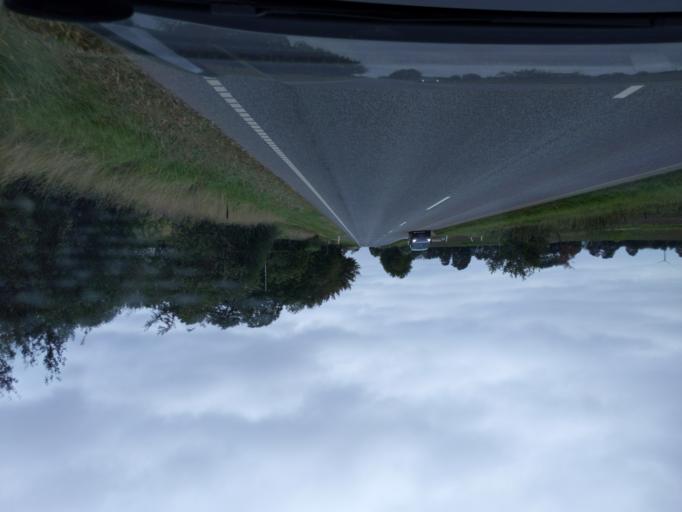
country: DK
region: Central Jutland
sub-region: Randers Kommune
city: Spentrup
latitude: 56.5322
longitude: 9.9123
